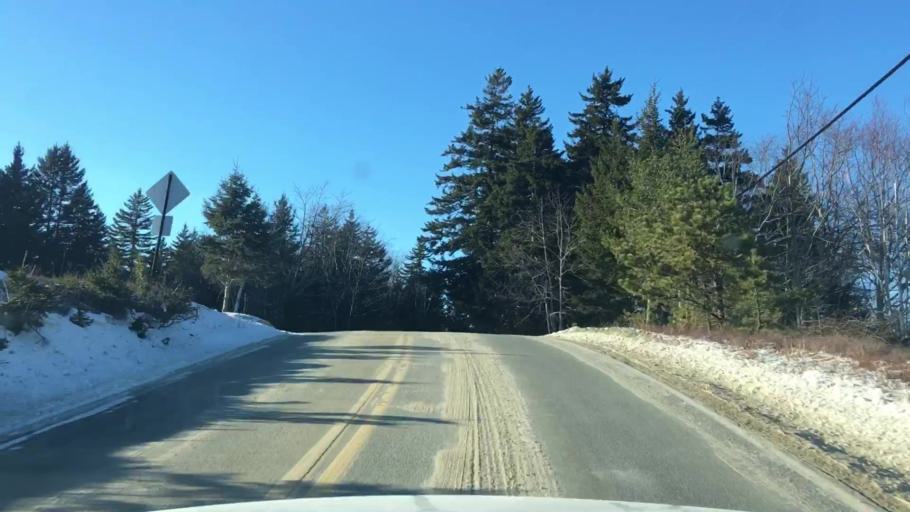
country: US
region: Maine
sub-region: Hancock County
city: Castine
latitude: 44.3660
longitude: -68.7518
